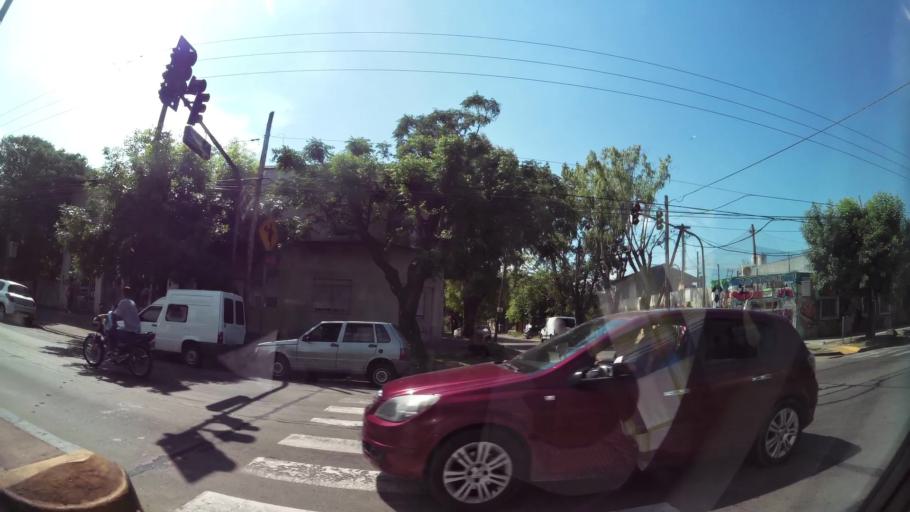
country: AR
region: Buenos Aires
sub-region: Partido de Tigre
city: Tigre
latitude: -34.4675
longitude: -58.5868
